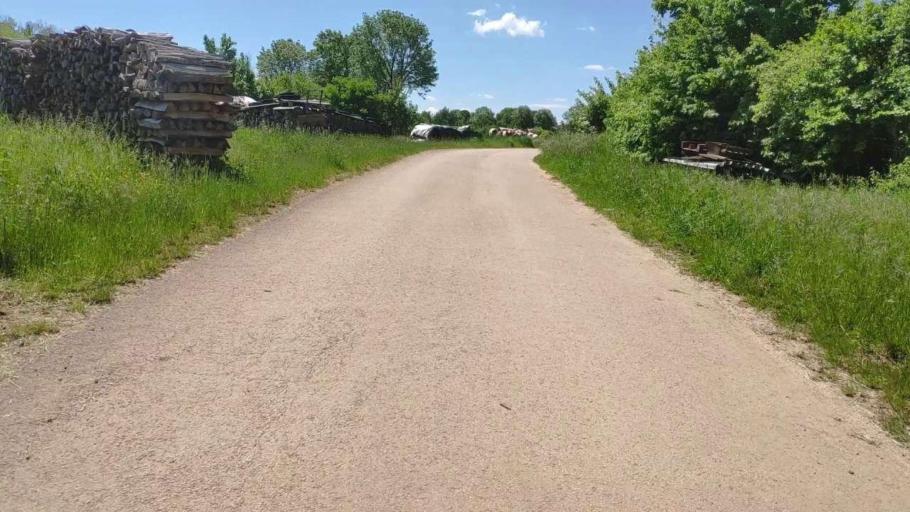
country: FR
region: Franche-Comte
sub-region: Departement du Jura
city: Poligny
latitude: 46.7313
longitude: 5.6965
